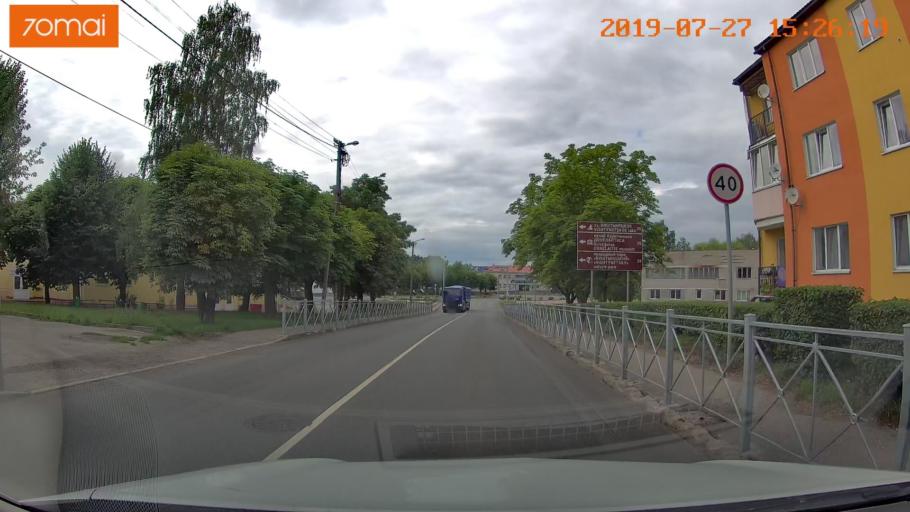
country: RU
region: Kaliningrad
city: Nesterov
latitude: 54.6310
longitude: 22.5739
